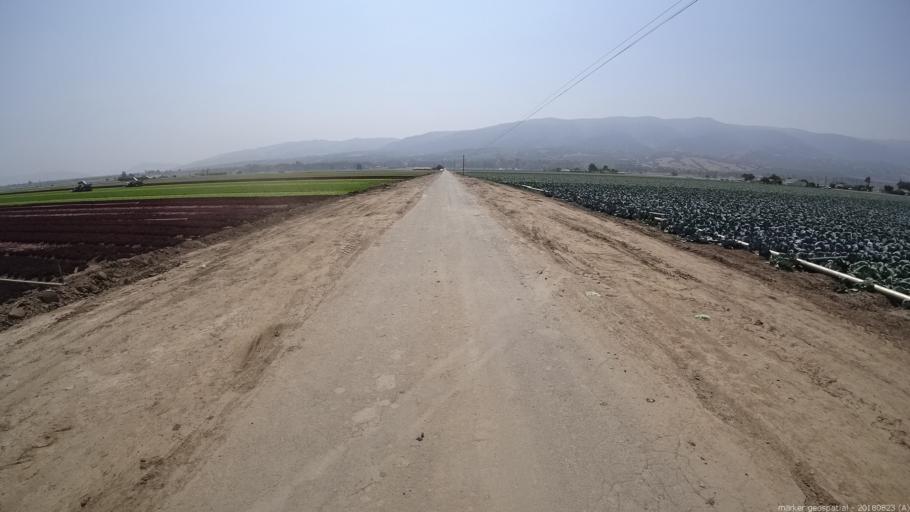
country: US
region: California
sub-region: Monterey County
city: Soledad
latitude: 36.3987
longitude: -121.3422
